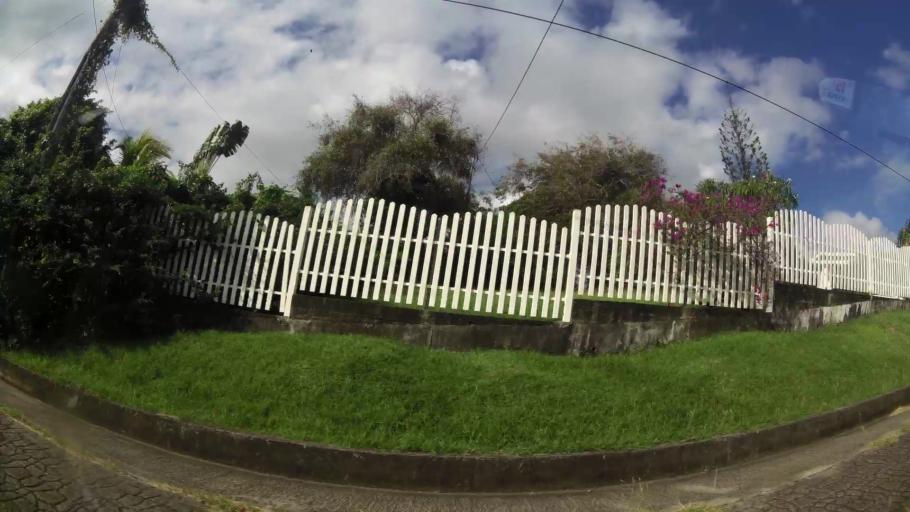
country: MQ
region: Martinique
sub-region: Martinique
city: Le Francois
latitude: 14.5980
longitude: -60.8741
